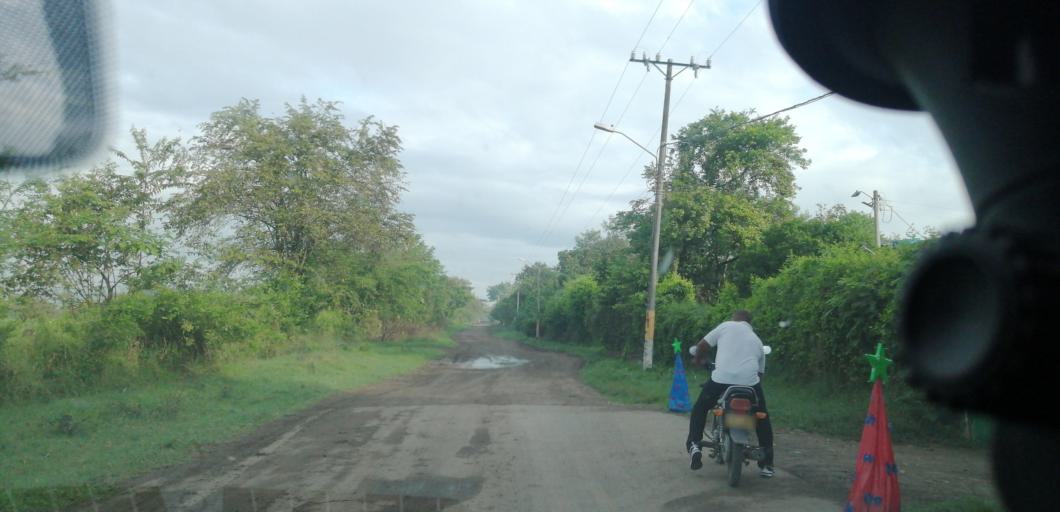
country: CO
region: Valle del Cauca
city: Palmira
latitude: 3.5400
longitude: -76.3595
